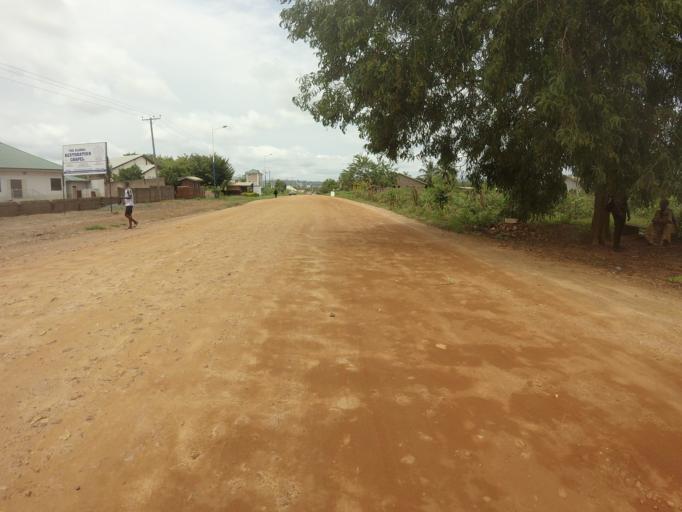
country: GH
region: Volta
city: Ho
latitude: 6.5804
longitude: 0.4634
